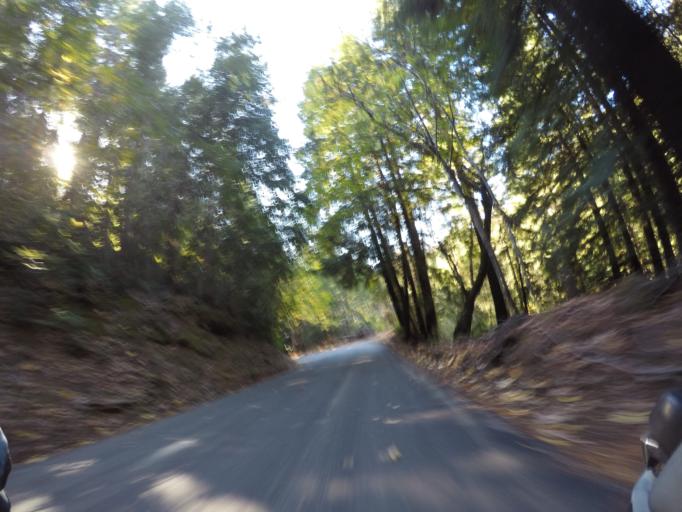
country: US
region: California
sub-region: Santa Clara County
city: Lexington Hills
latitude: 37.1491
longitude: -122.0158
